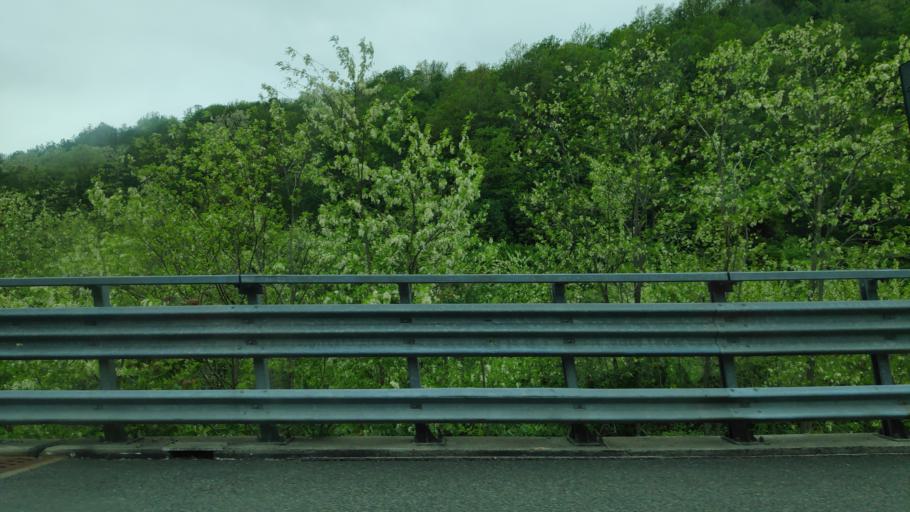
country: IT
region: Tuscany
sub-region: Provincia di Massa-Carrara
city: Villafranca in Lunigiana
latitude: 44.2737
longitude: 9.9519
